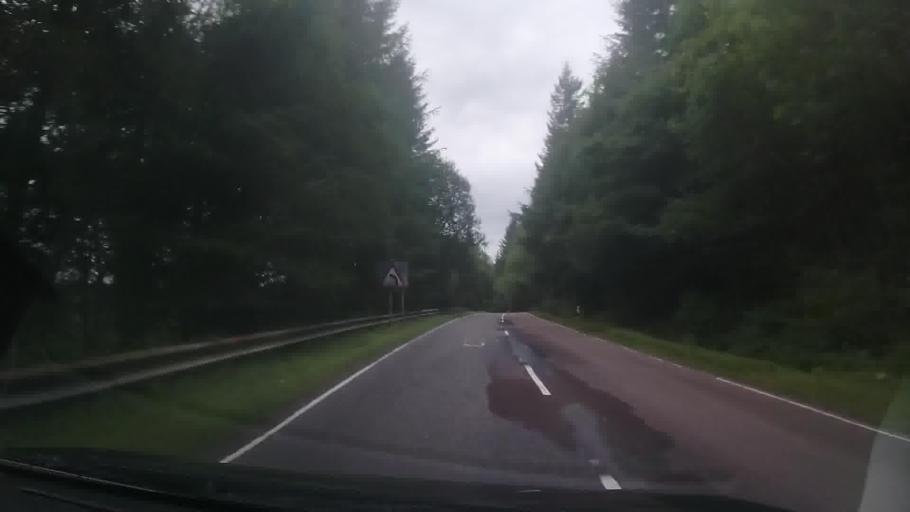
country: GB
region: Scotland
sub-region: Argyll and Bute
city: Garelochhead
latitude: 56.2557
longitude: -5.0913
